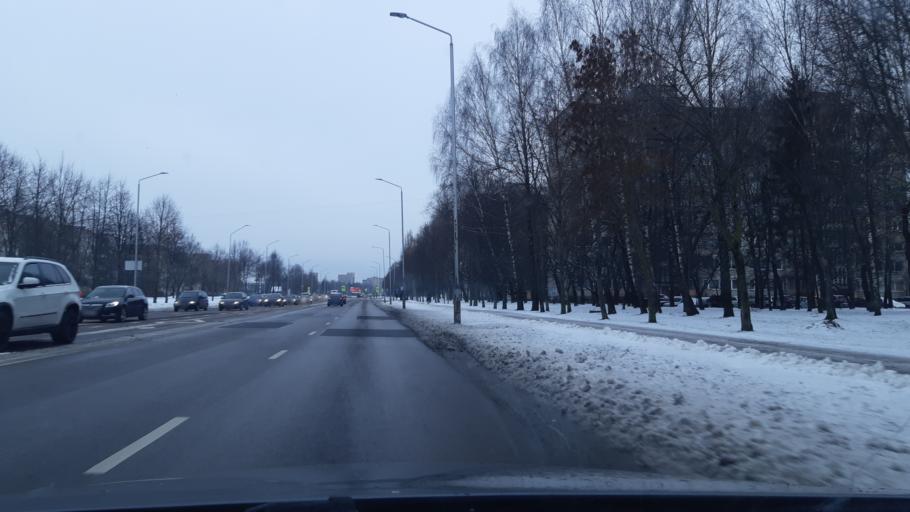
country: LT
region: Kauno apskritis
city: Dainava (Kaunas)
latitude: 54.9265
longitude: 23.9744
